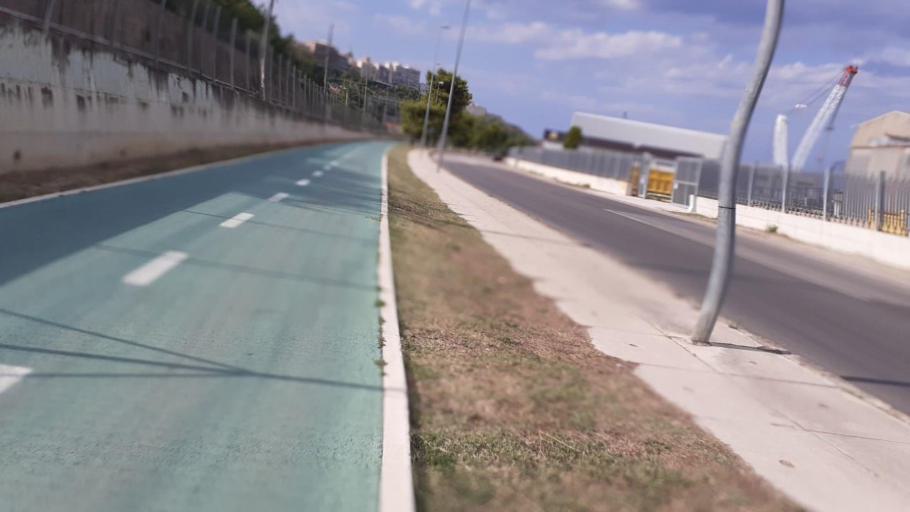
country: IT
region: Abruzzo
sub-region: Provincia di Chieti
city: Ortona
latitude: 42.3483
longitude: 14.4089
